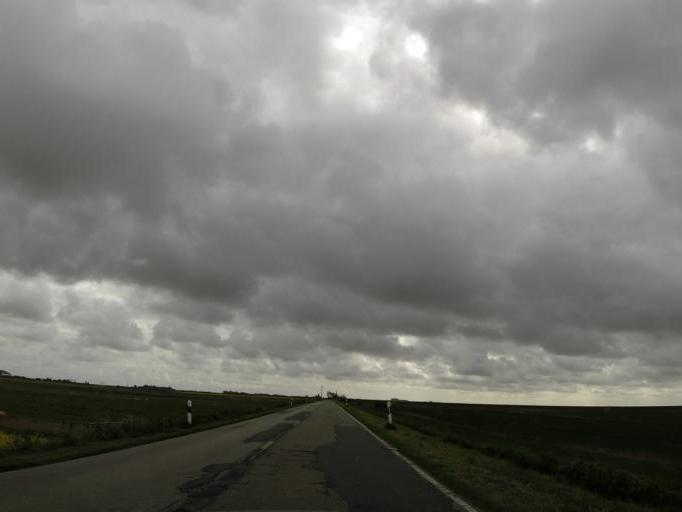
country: DE
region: Schleswig-Holstein
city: Galmsbull
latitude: 54.7452
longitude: 8.7328
